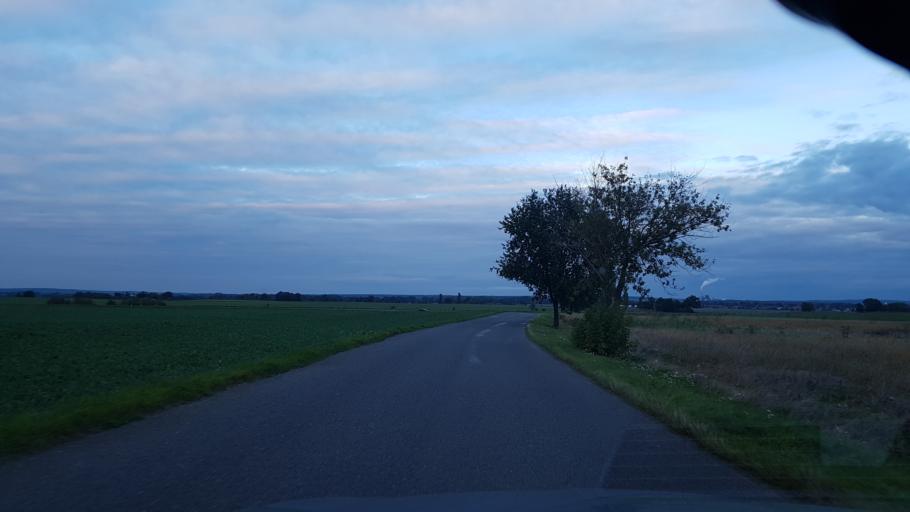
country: DE
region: Saxony
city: Ebersbach
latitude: 51.2626
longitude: 13.5956
